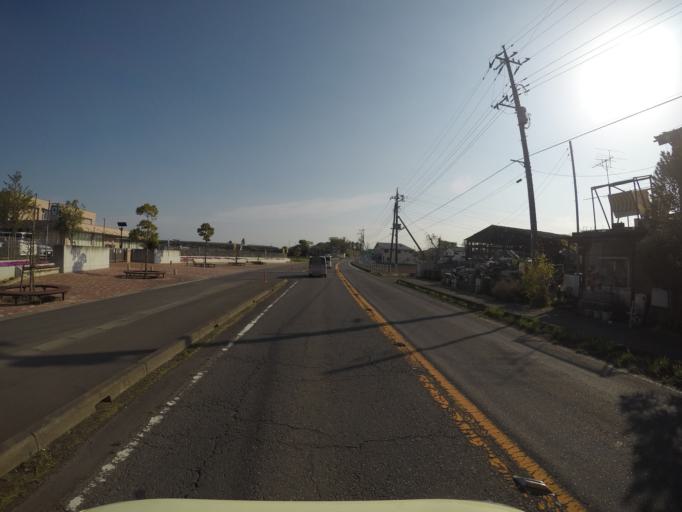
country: JP
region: Ibaraki
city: Ishige
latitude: 36.2013
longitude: 139.9759
